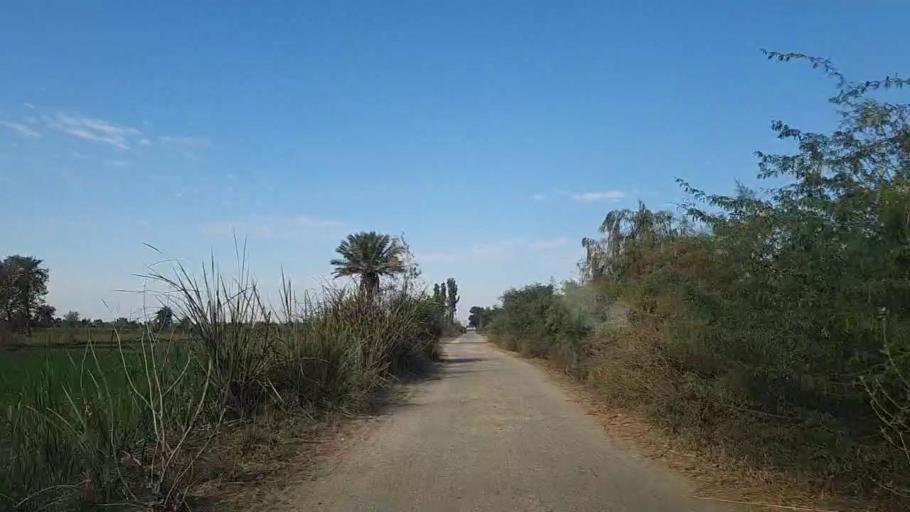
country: PK
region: Sindh
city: Khadro
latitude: 26.2911
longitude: 68.8201
